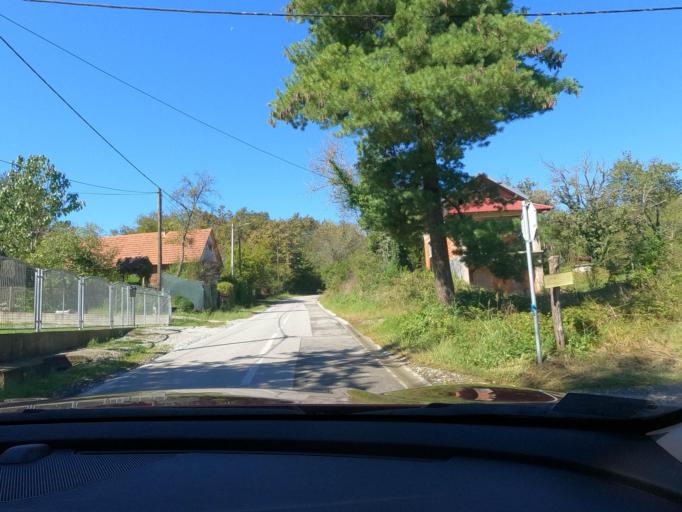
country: HR
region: Sisacko-Moslavacka
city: Petrinja
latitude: 45.4666
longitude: 16.2855
